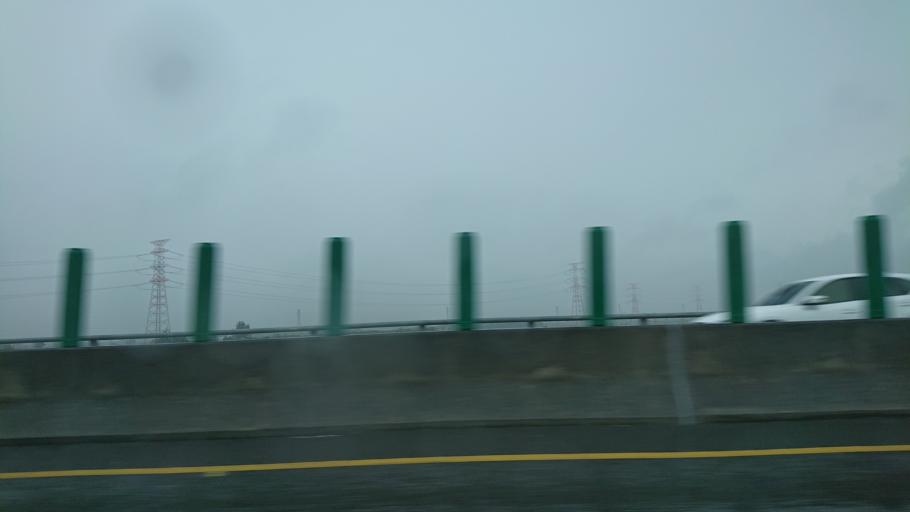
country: TW
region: Taiwan
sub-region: Yunlin
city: Douliu
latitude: 23.7726
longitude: 120.2724
